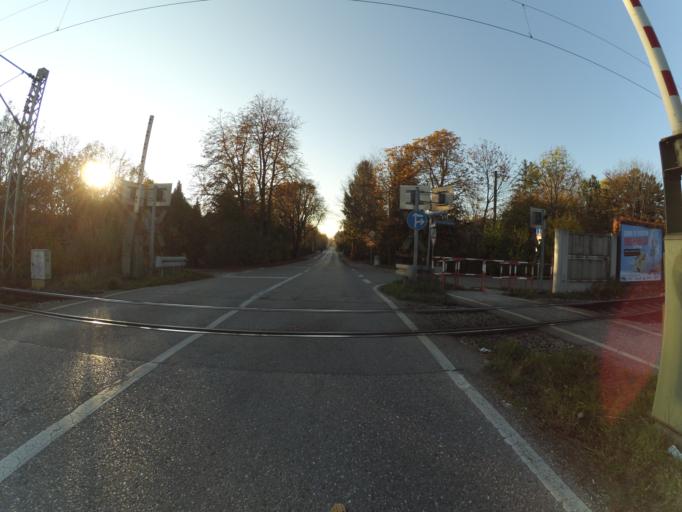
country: DE
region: Bavaria
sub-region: Upper Bavaria
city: Oberschleissheim
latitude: 48.1922
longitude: 11.5412
